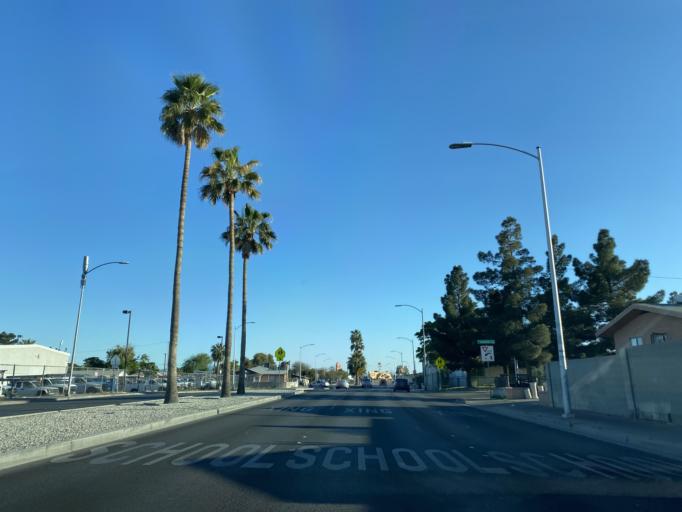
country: US
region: Nevada
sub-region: Clark County
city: Las Vegas
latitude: 36.1636
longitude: -115.1159
